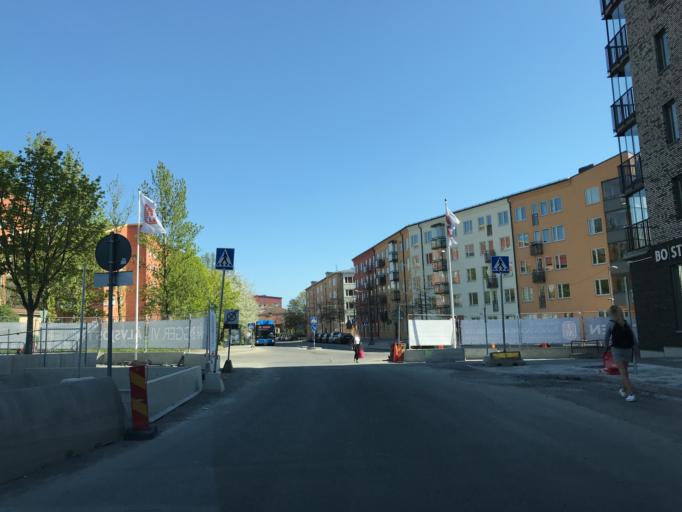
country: SE
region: Stockholm
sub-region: Huddinge Kommun
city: Huddinge
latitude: 59.2807
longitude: 18.0043
